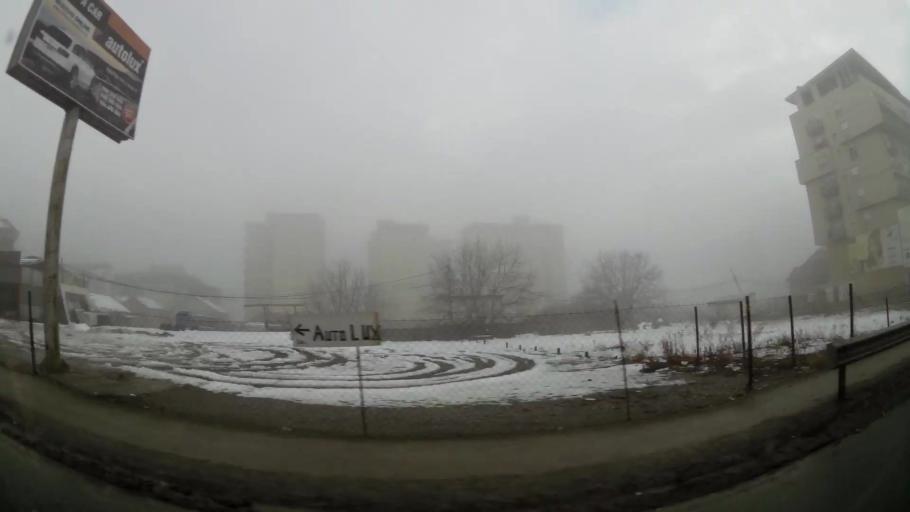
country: XK
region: Pristina
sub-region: Komuna e Prishtines
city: Pristina
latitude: 42.6486
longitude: 21.1531
